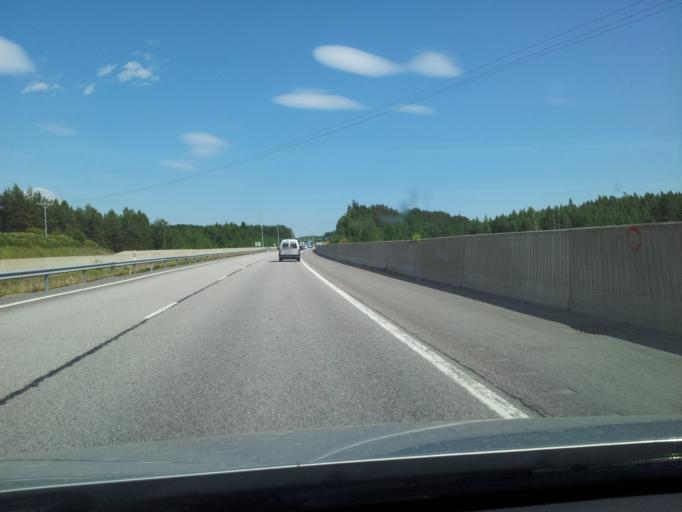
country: FI
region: Uusimaa
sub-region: Loviisa
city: Perna
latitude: 60.4932
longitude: 25.9348
